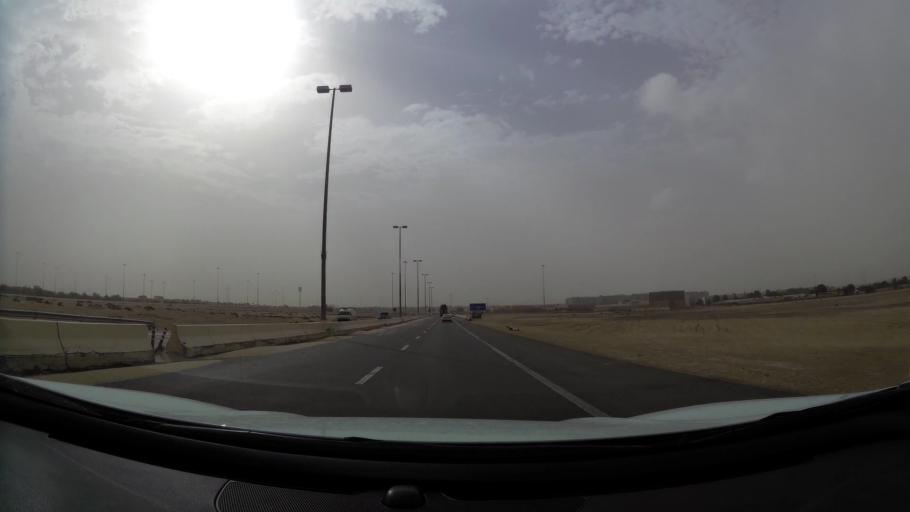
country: AE
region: Abu Dhabi
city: Abu Dhabi
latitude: 24.4665
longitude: 54.6731
